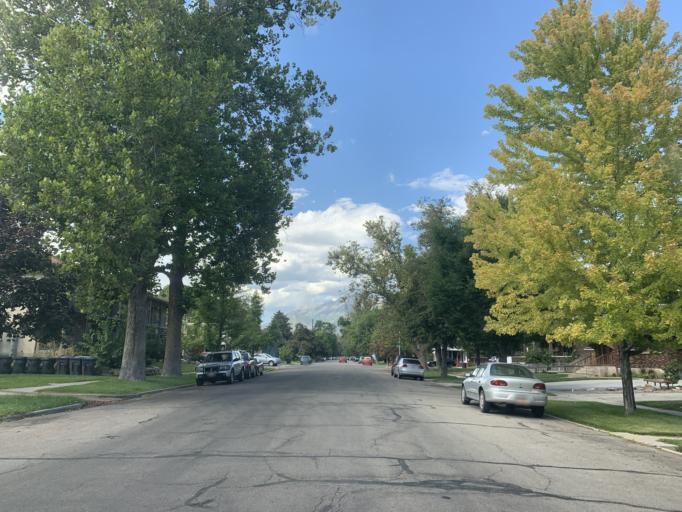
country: US
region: Utah
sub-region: Utah County
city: Provo
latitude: 40.2358
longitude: -111.6517
